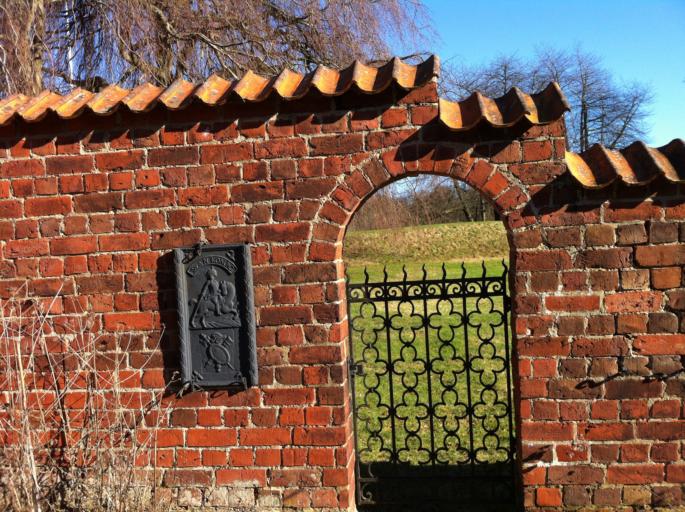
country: SE
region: Skane
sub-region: Svedala Kommun
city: Klagerup
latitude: 55.5653
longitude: 13.2095
